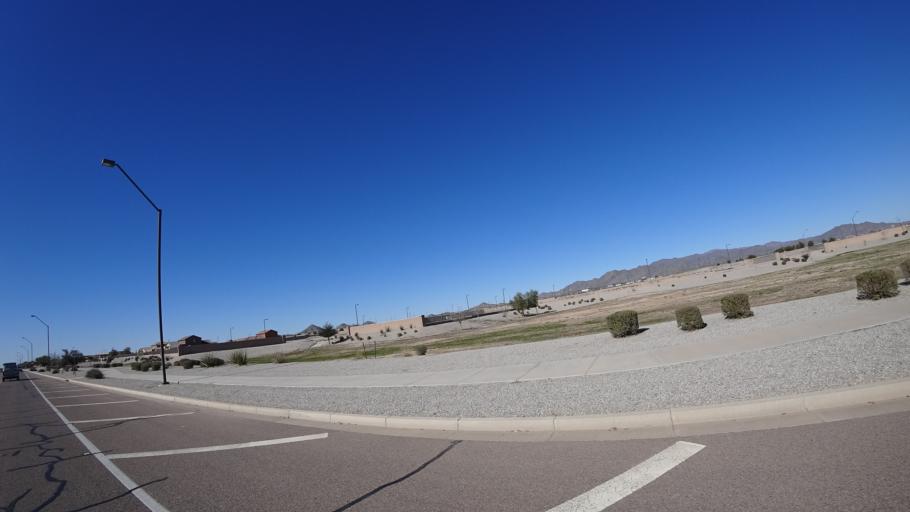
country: US
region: Arizona
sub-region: Maricopa County
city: Buckeye
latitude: 33.4066
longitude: -112.5747
